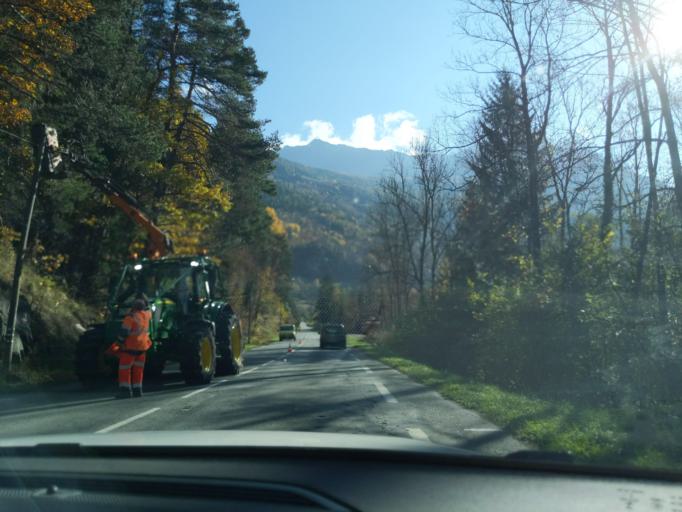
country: FR
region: Rhone-Alpes
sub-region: Departement de la Savoie
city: Seez
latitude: 45.5993
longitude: 6.8704
